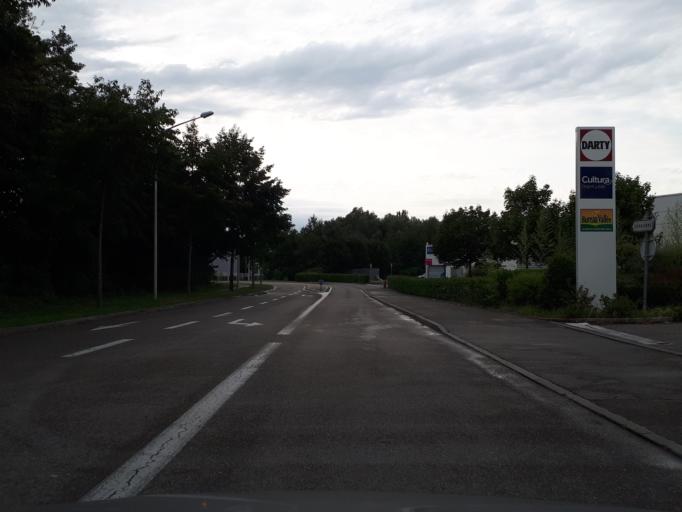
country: FR
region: Rhone-Alpes
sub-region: Departement de l'Isere
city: Domarin
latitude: 45.5896
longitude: 5.2521
